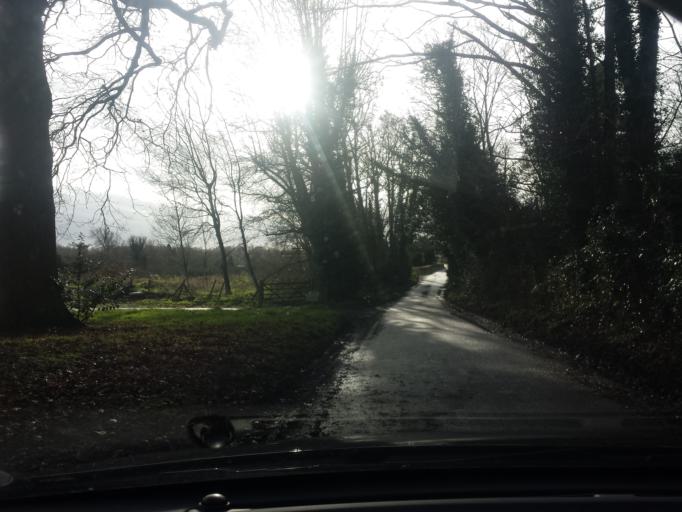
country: GB
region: England
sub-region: Essex
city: Alresford
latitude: 51.8971
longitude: 1.0282
